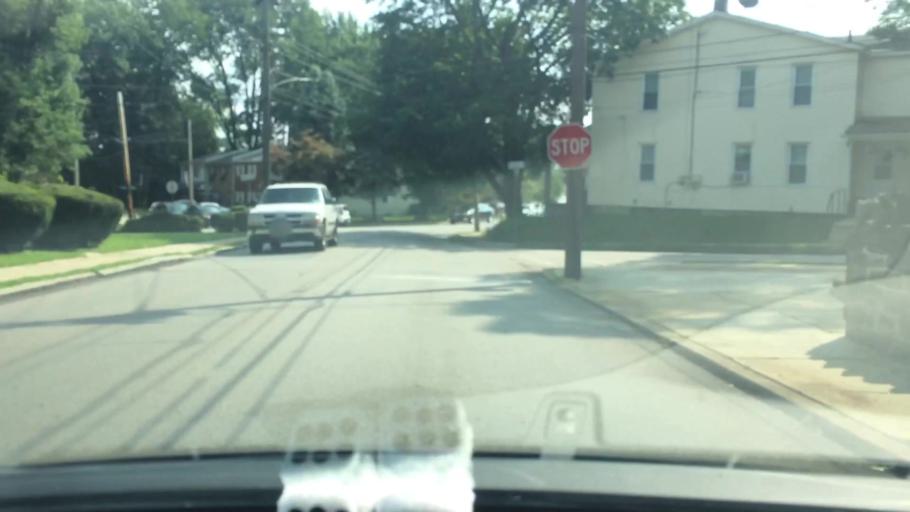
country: US
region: Pennsylvania
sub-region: Delaware County
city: Morton
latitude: 39.9111
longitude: -75.3248
